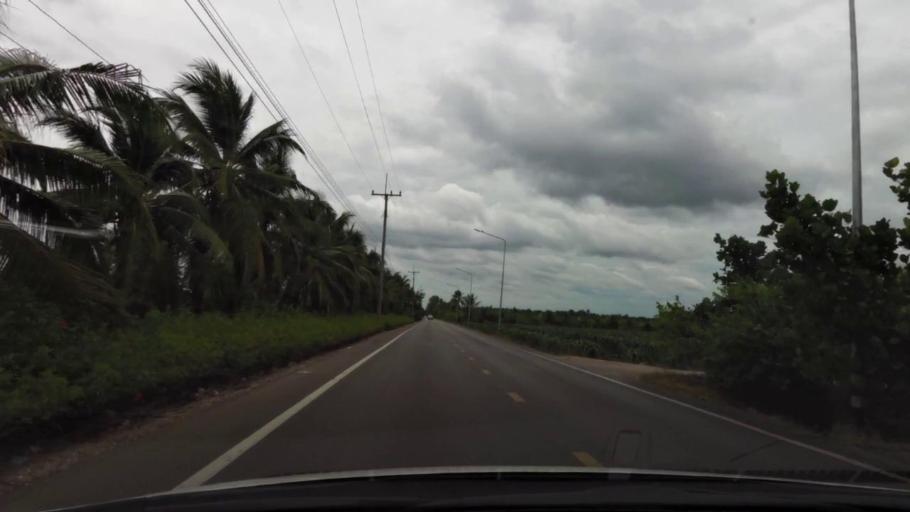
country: TH
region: Ratchaburi
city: Damnoen Saduak
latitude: 13.5586
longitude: 100.0144
